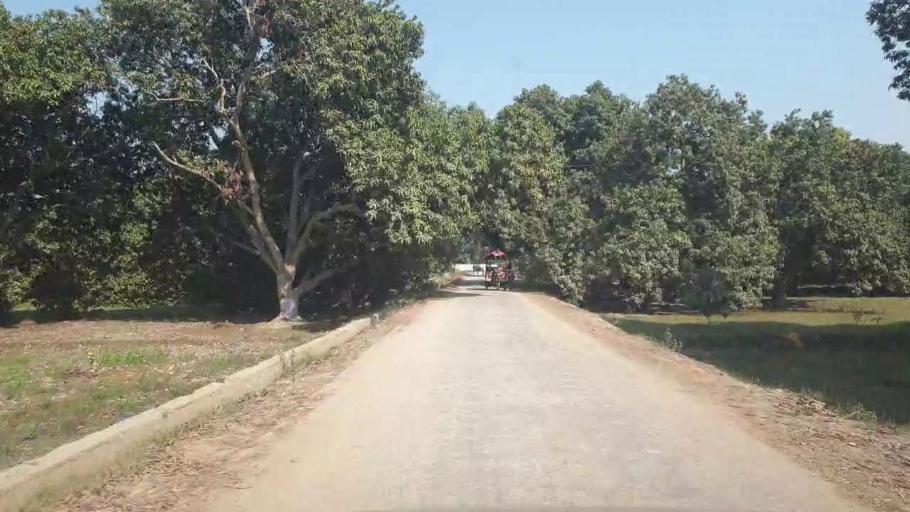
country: PK
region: Sindh
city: Tando Allahyar
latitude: 25.4789
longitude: 68.7840
